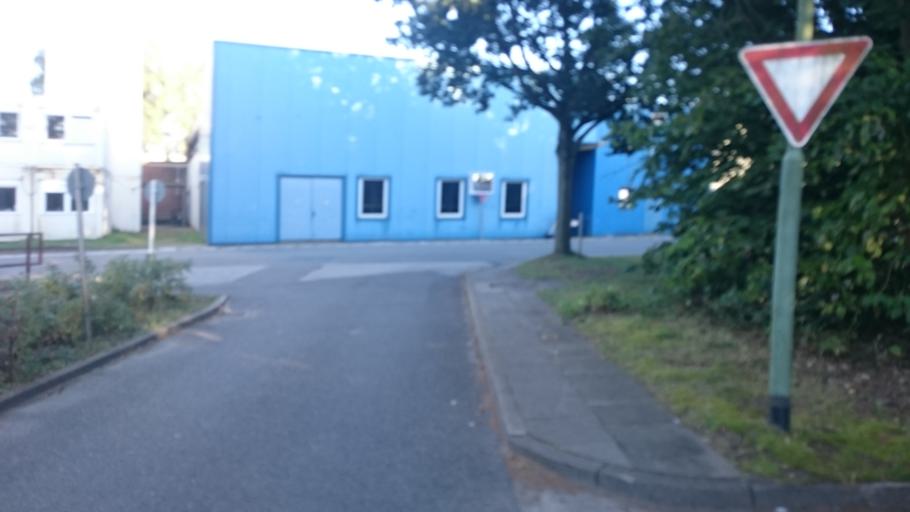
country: DE
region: Hamburg
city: Eidelstedt
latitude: 53.5759
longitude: 9.8820
